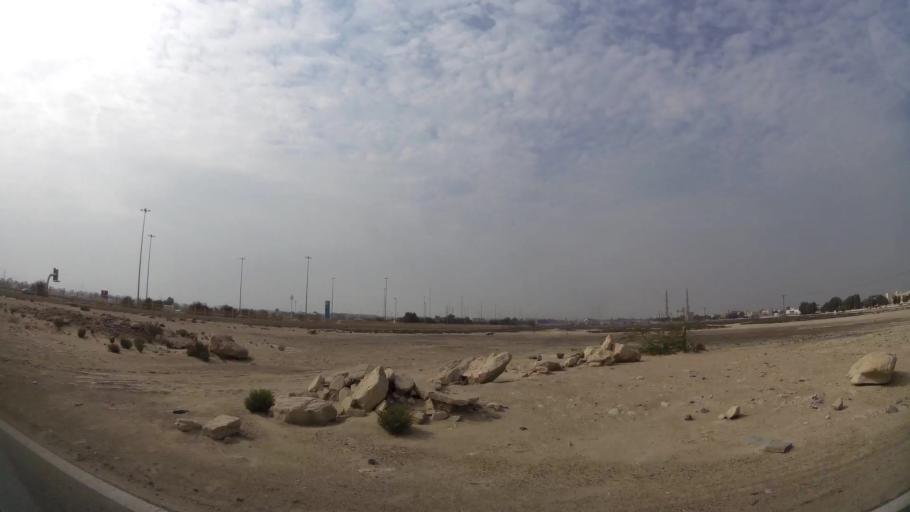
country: AE
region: Abu Dhabi
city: Abu Dhabi
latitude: 24.6771
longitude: 54.7645
